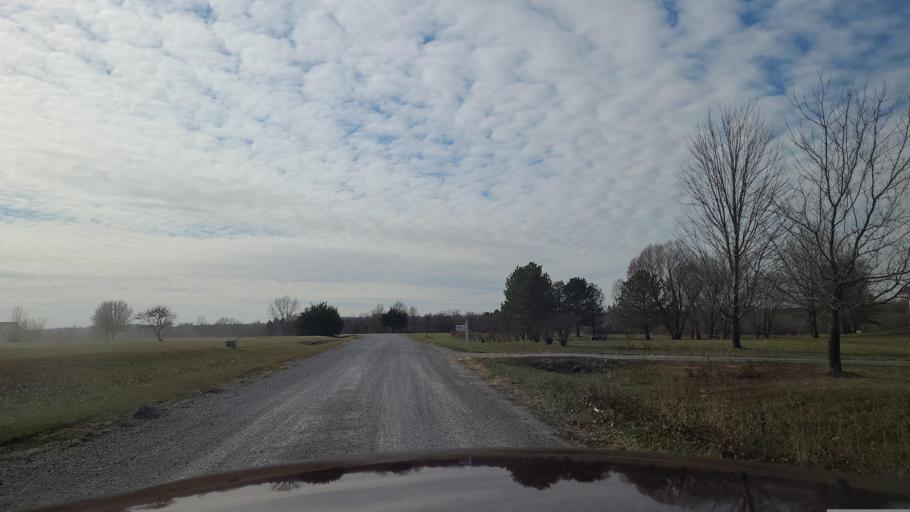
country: US
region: Kansas
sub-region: Douglas County
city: Eudora
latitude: 38.9168
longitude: -95.1067
